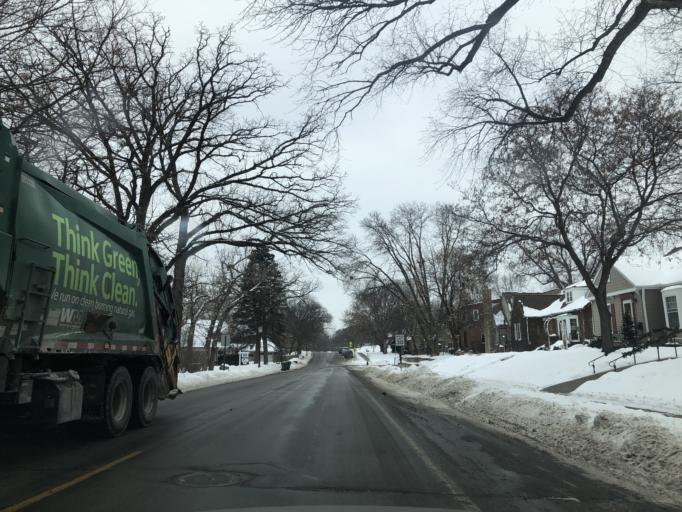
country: US
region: Minnesota
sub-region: Hennepin County
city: Robbinsdale
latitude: 45.0284
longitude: -93.3232
